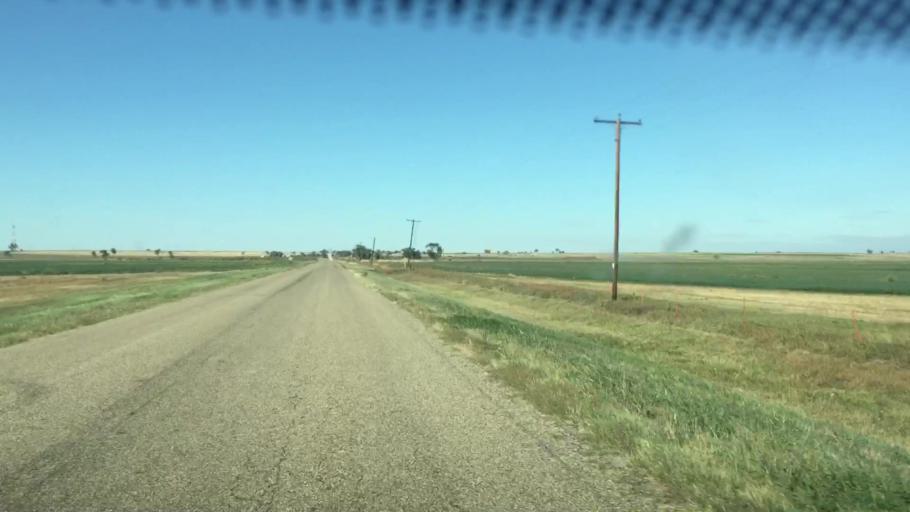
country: US
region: Colorado
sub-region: Prowers County
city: Lamar
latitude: 38.1019
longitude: -102.5215
